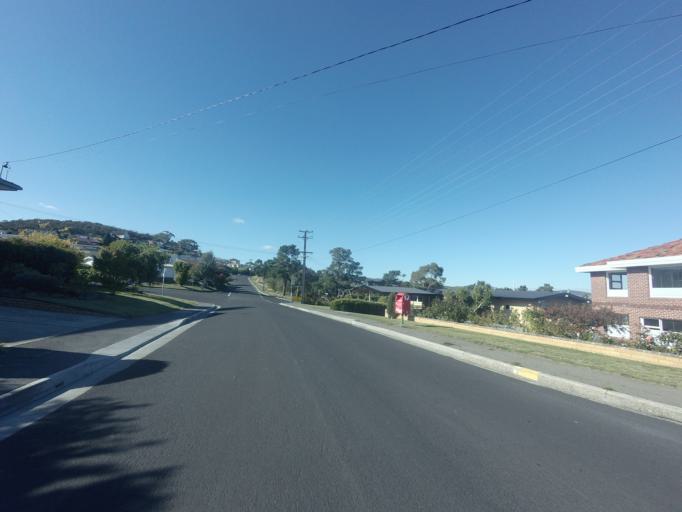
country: AU
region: Tasmania
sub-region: Clarence
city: Bellerive
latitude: -42.8735
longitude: 147.3553
